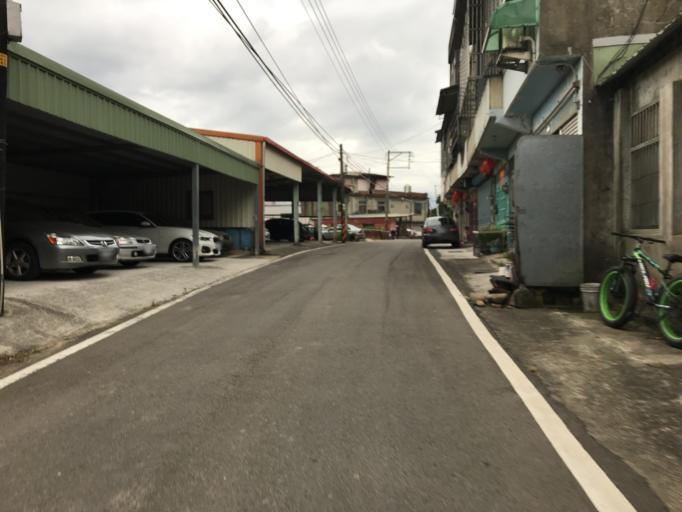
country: TW
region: Taiwan
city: Daxi
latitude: 24.7818
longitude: 121.1750
